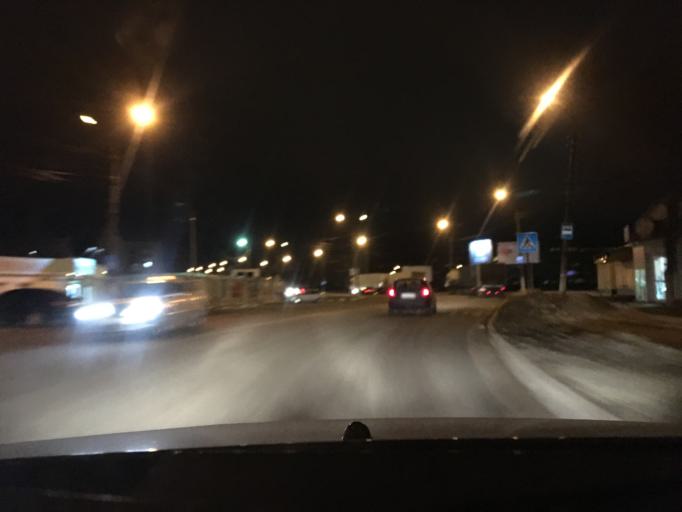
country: RU
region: Tula
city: Shchekino
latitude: 54.0206
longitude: 37.5030
